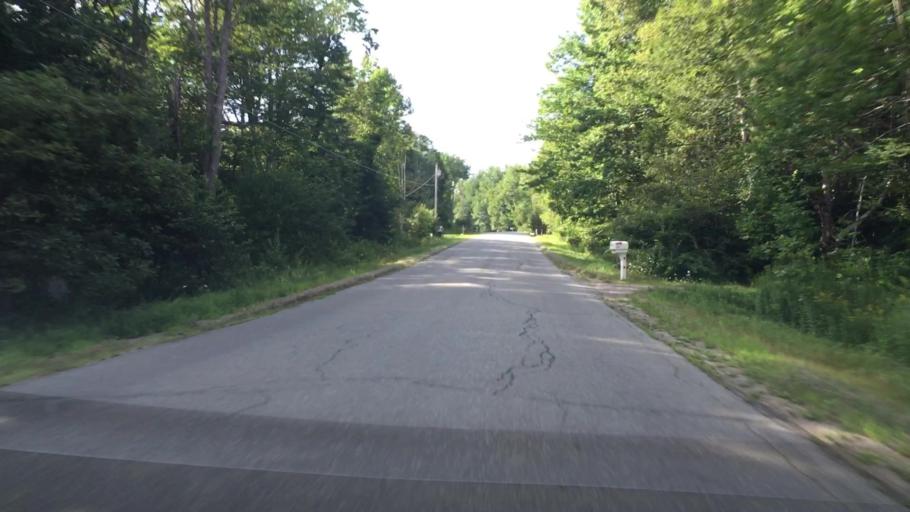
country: US
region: Maine
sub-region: Waldo County
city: Stockton Springs
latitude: 44.4909
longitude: -68.8675
